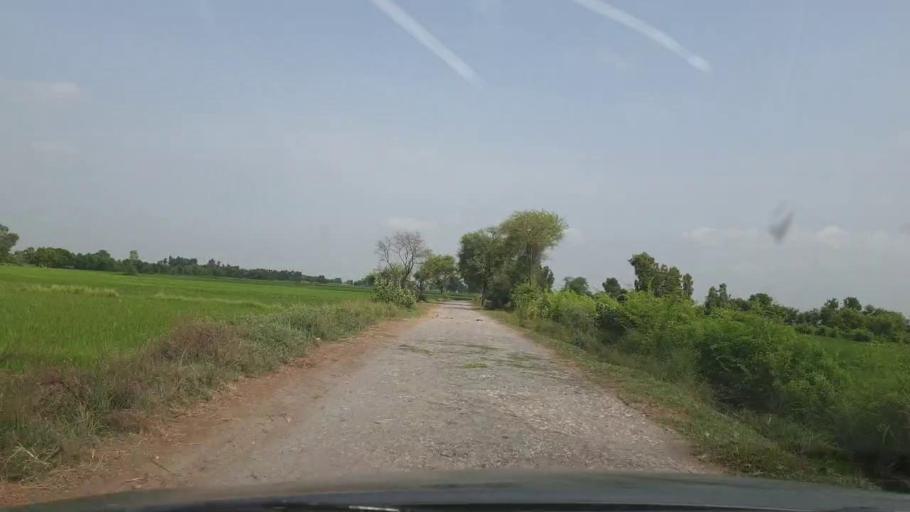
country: PK
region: Sindh
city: Ratodero
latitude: 27.8507
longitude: 68.3002
